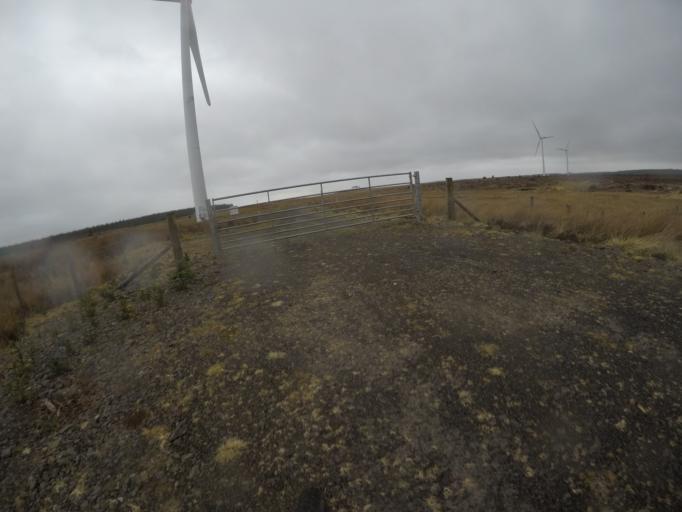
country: GB
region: Scotland
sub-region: East Ayrshire
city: Newmilns
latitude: 55.6354
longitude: -4.3287
